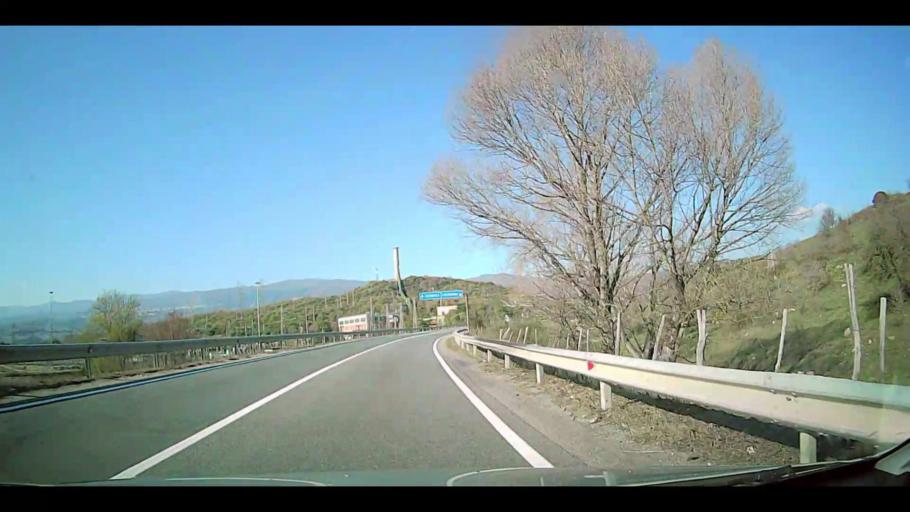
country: IT
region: Calabria
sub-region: Provincia di Crotone
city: Roccabernarda
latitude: 39.1847
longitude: 16.8369
